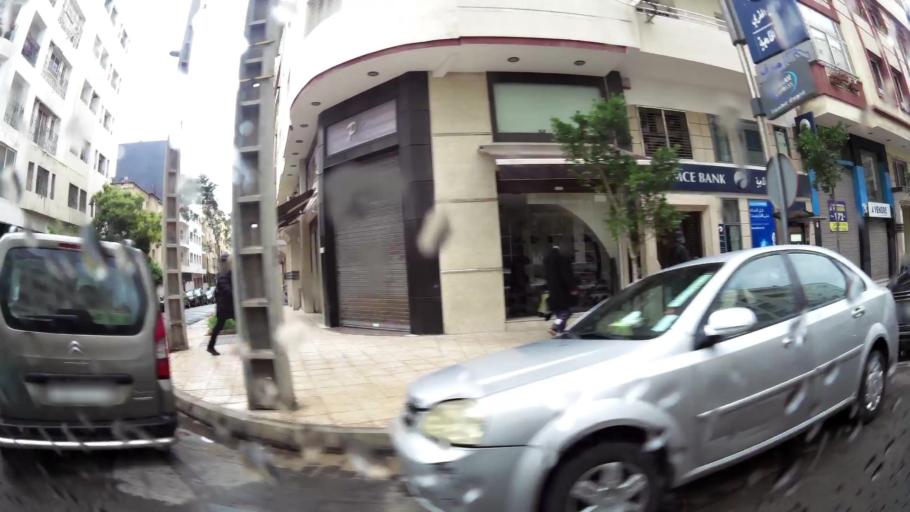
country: MA
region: Grand Casablanca
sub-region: Casablanca
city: Casablanca
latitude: 33.5734
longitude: -7.6126
